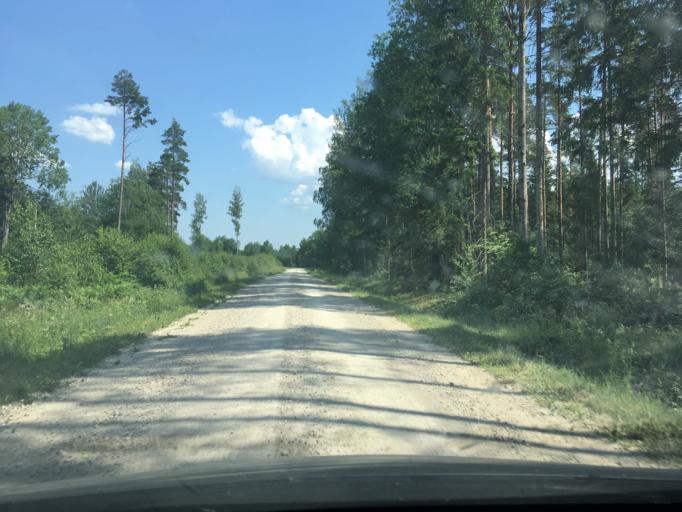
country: EE
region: Raplamaa
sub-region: Maerjamaa vald
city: Marjamaa
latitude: 58.8063
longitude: 24.4272
